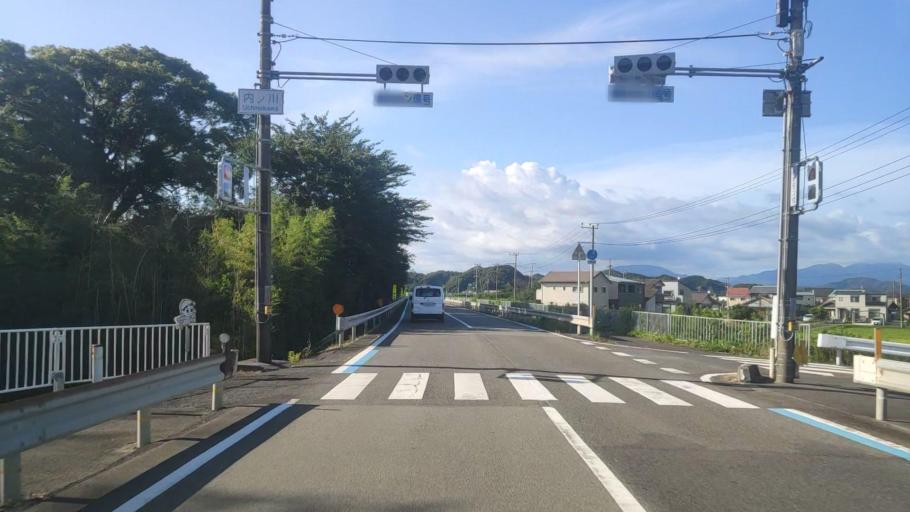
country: JP
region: Wakayama
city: Tanabe
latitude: 33.6746
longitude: 135.4078
